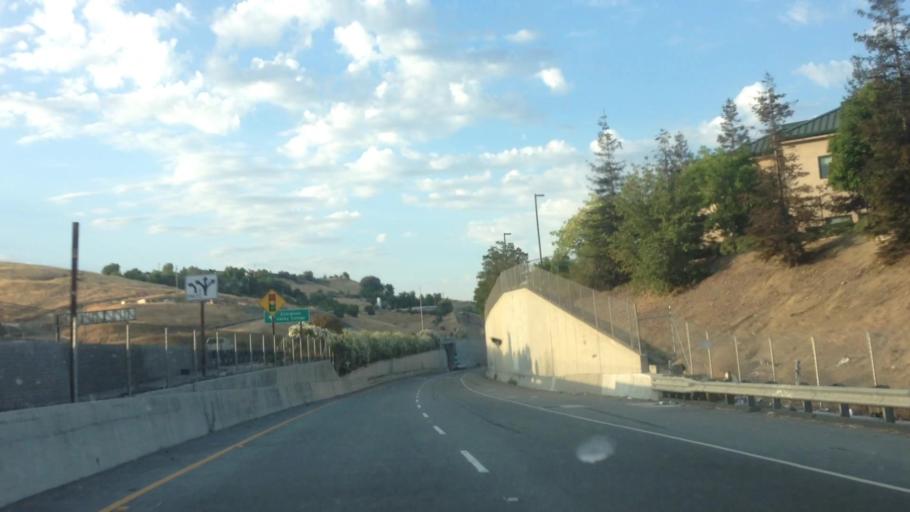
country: US
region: California
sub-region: Santa Clara County
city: Seven Trees
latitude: 37.2967
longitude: -121.8112
